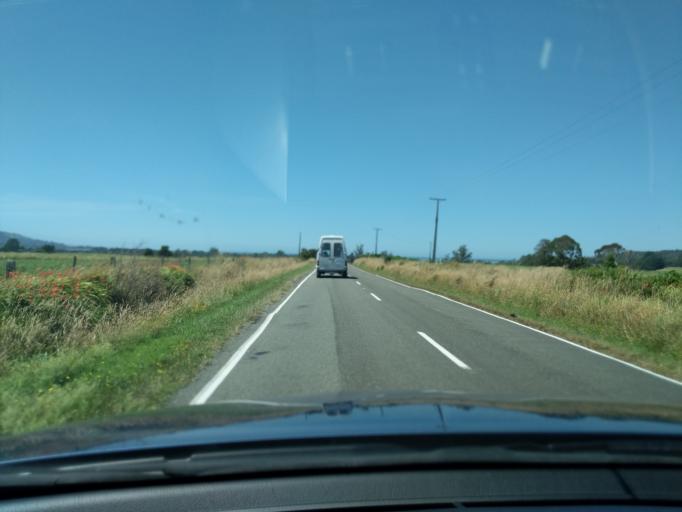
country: NZ
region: Tasman
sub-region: Tasman District
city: Takaka
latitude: -40.6889
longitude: 172.6469
